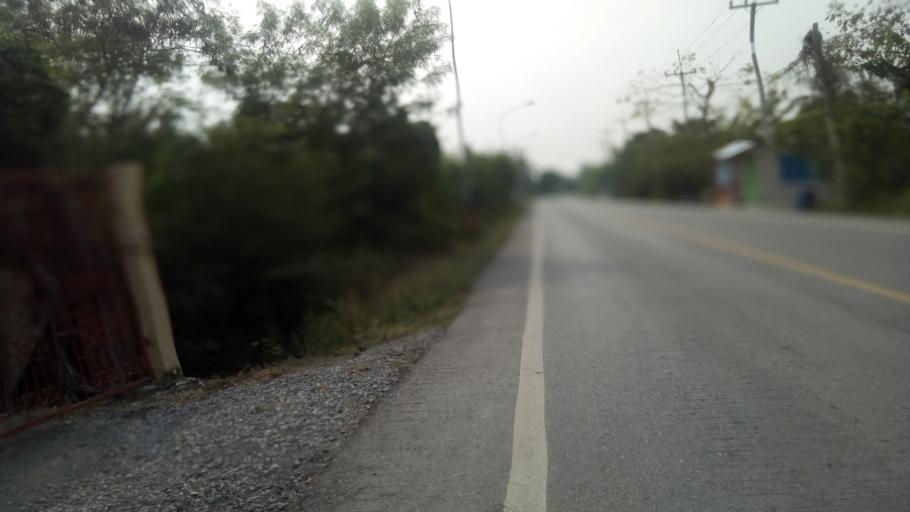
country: TH
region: Pathum Thani
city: Ban Rangsit
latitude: 14.0360
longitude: 100.8243
